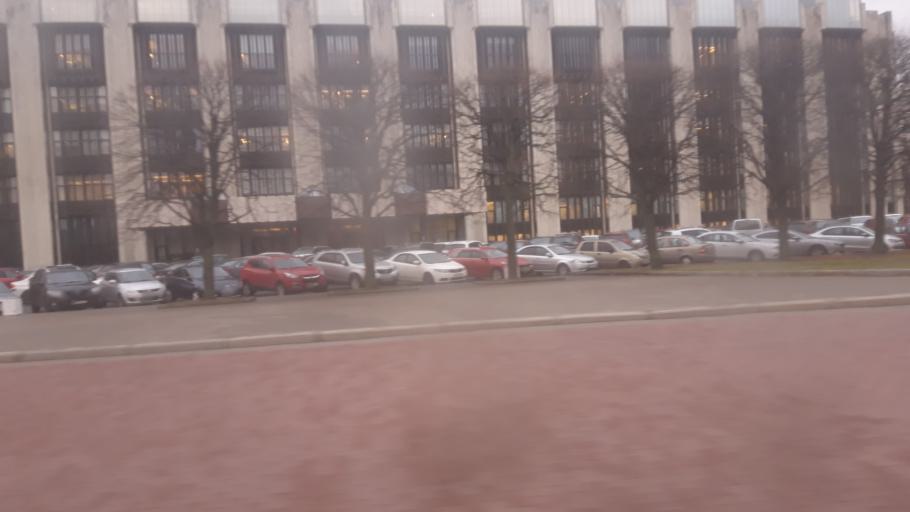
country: RU
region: St.-Petersburg
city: Kupchino
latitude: 59.8428
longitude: 30.3236
